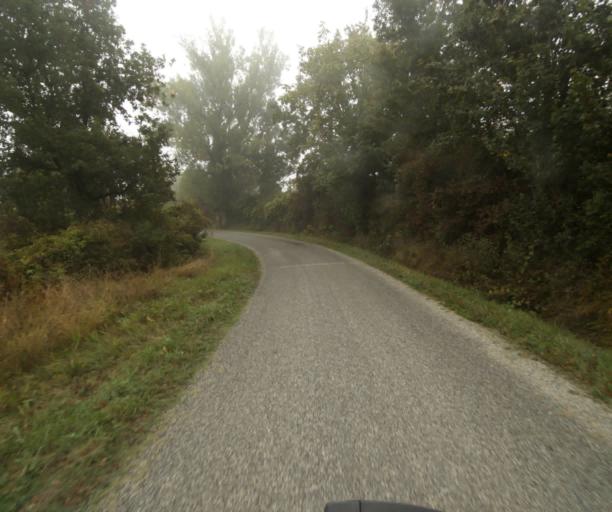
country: FR
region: Midi-Pyrenees
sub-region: Departement de la Haute-Garonne
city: Villemur-sur-Tarn
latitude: 43.8914
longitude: 1.4859
